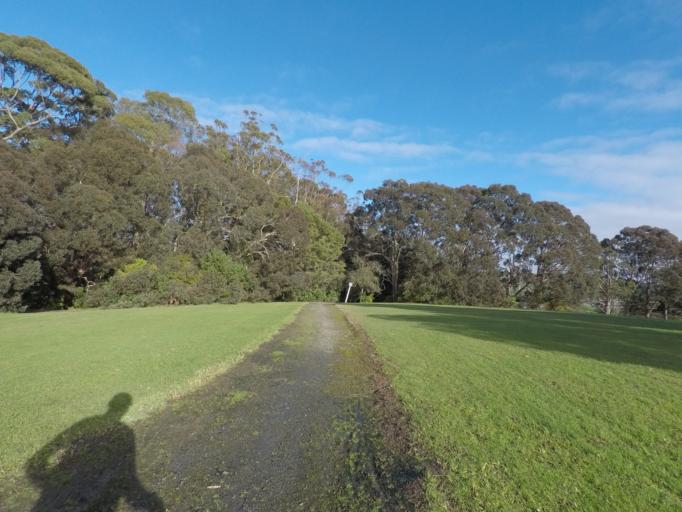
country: NZ
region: Auckland
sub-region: Auckland
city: Warkworth
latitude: -36.4219
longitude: 174.7220
